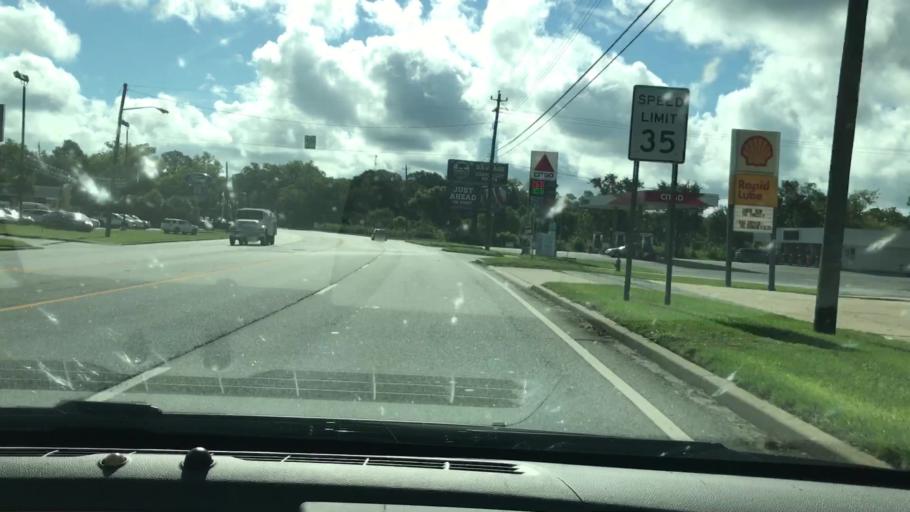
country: US
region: Georgia
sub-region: Worth County
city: Sylvester
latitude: 31.5316
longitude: -83.8522
